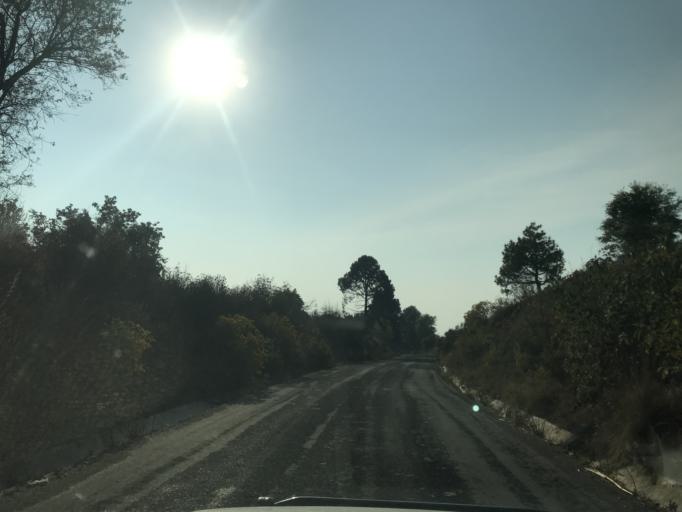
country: MX
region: Puebla
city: San Nicolas de los Ranchos
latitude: 19.0864
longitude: -98.5288
